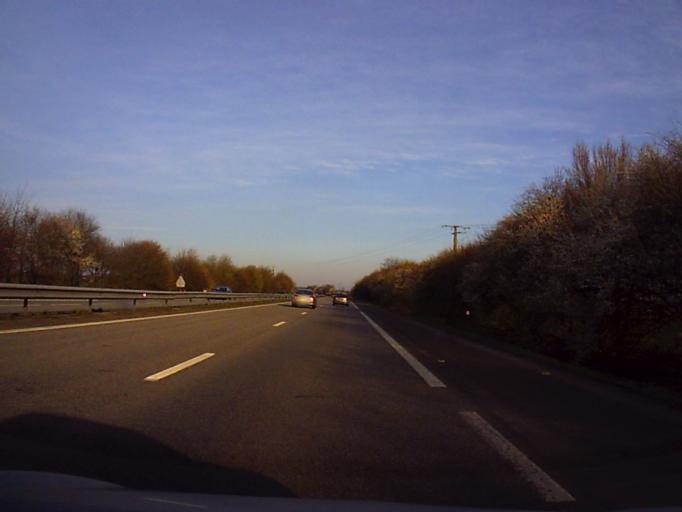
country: FR
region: Brittany
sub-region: Departement d'Ille-et-Vilaine
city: Monterfil
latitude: 48.0306
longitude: -2.0050
